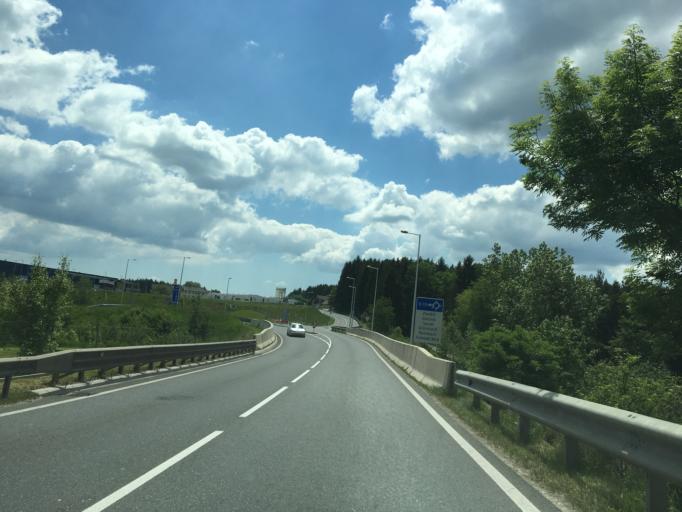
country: AT
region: Upper Austria
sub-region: Politischer Bezirk Freistadt
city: Freistadt
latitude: 48.4854
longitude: 14.4970
